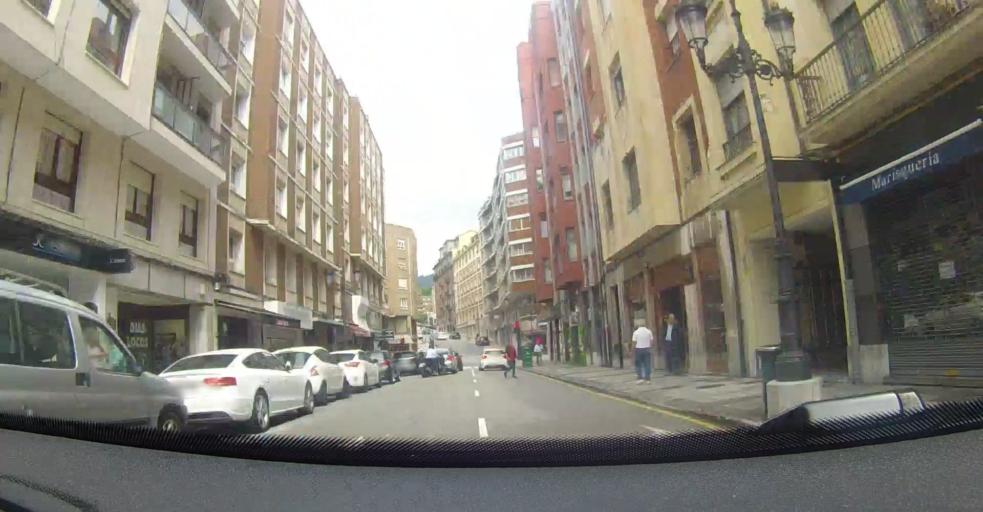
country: ES
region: Asturias
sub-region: Province of Asturias
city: Oviedo
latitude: 43.3645
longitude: -5.8536
